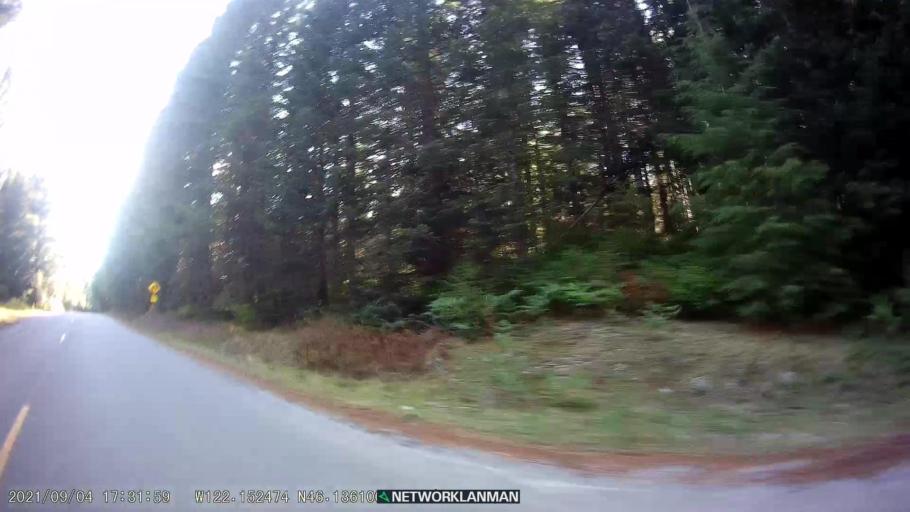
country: US
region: Washington
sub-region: Clark County
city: Yacolt
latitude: 46.1360
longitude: -122.1527
